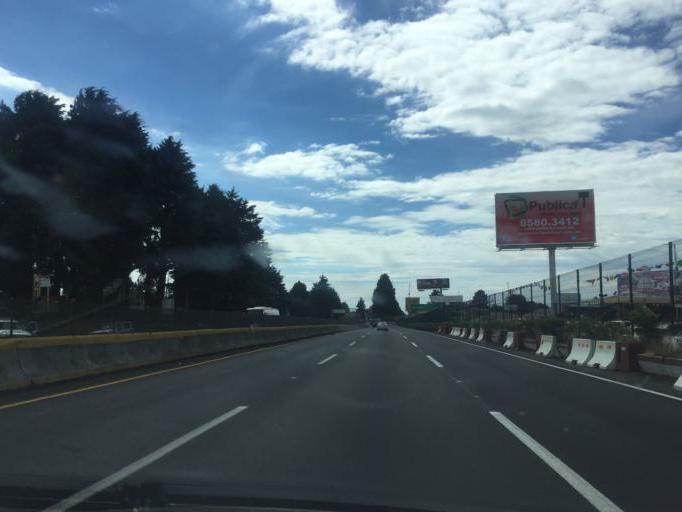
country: MX
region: Morelos
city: Tres Marias
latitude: 19.0528
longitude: -99.2416
